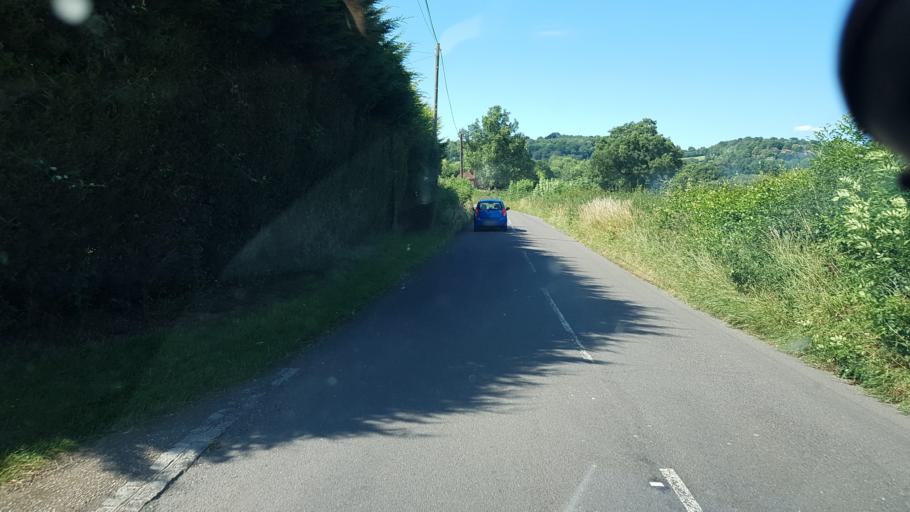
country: GB
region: England
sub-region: Kent
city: Edenbridge
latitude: 51.2274
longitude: 0.0731
